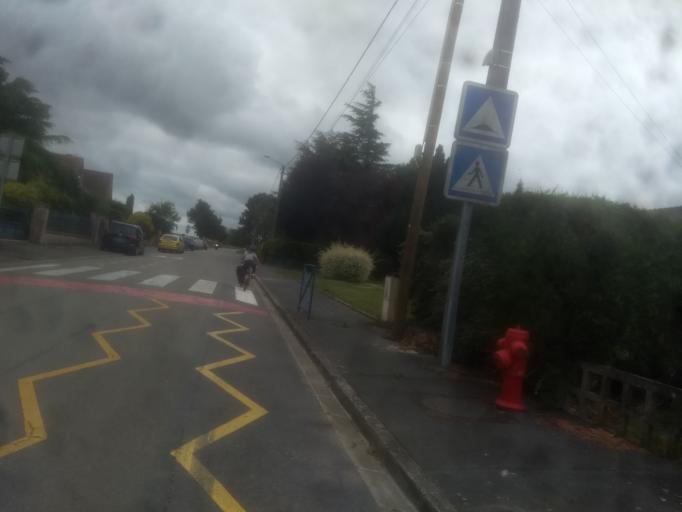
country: FR
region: Nord-Pas-de-Calais
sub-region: Departement du Pas-de-Calais
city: Saint-Nicolas
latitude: 50.3190
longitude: 2.7851
